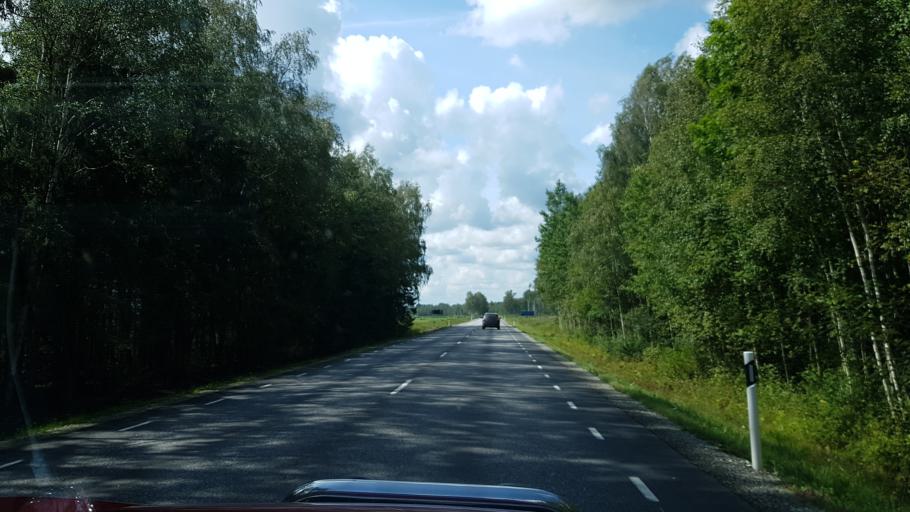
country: EE
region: Raplamaa
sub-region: Maerjamaa vald
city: Marjamaa
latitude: 58.9447
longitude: 24.5781
